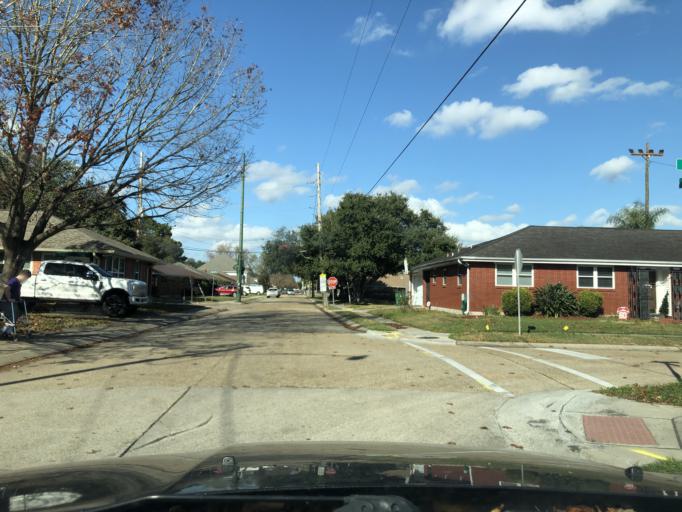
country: US
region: Louisiana
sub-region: Jefferson Parish
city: Metairie Terrace
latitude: 29.9874
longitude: -90.1645
